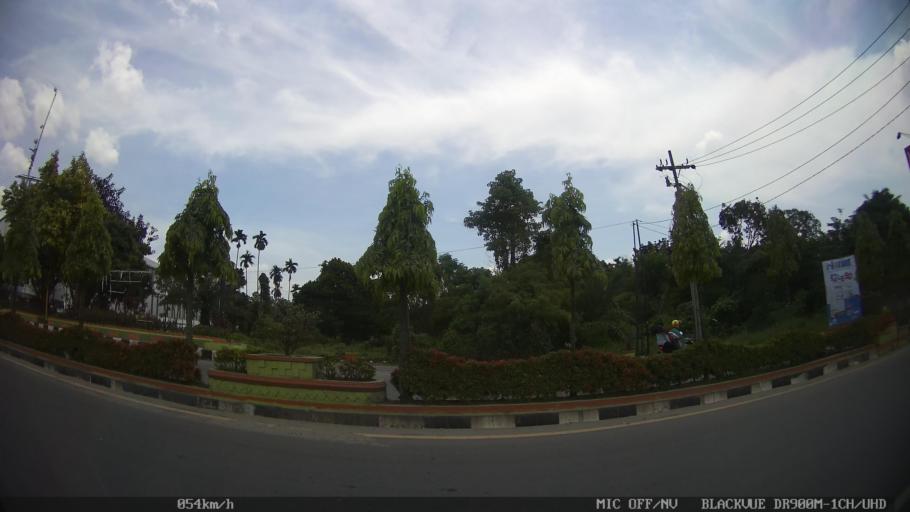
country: ID
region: North Sumatra
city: Binjai
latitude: 3.6037
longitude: 98.5354
